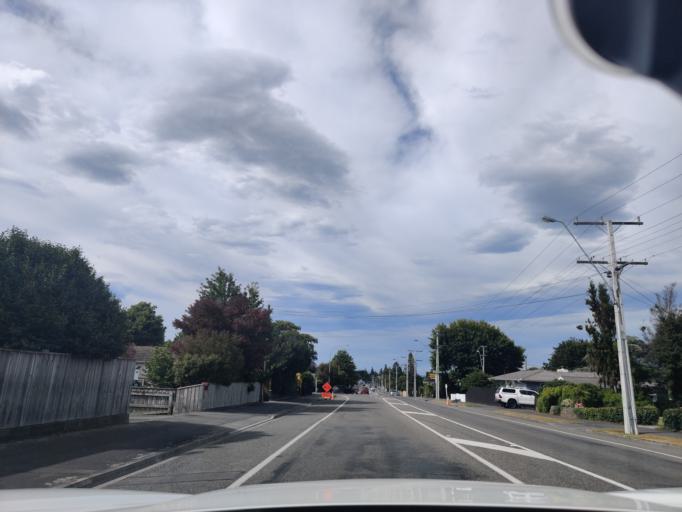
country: NZ
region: Wellington
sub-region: Masterton District
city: Masterton
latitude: -40.9386
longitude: 175.6706
